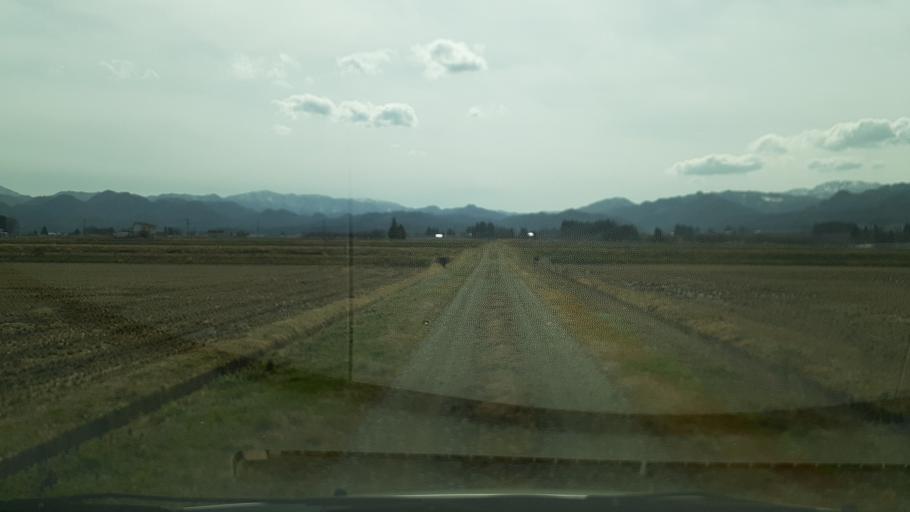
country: JP
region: Fukushima
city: Kitakata
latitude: 37.4649
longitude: 139.8280
